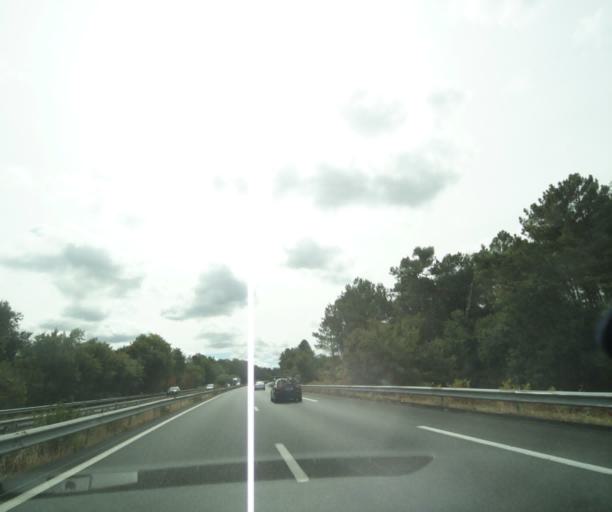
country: FR
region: Aquitaine
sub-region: Departement de la Gironde
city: Reignac
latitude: 45.2205
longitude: -0.5096
